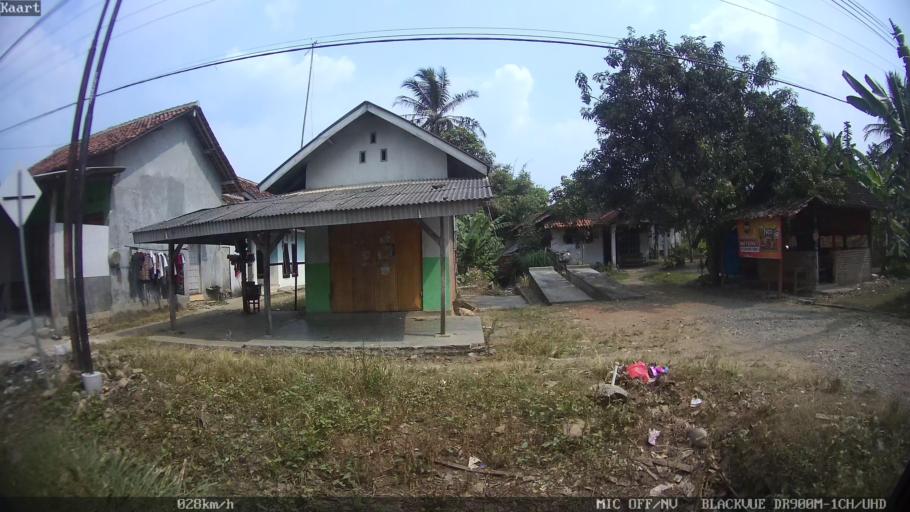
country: ID
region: Lampung
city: Pringsewu
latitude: -5.3519
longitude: 105.0199
